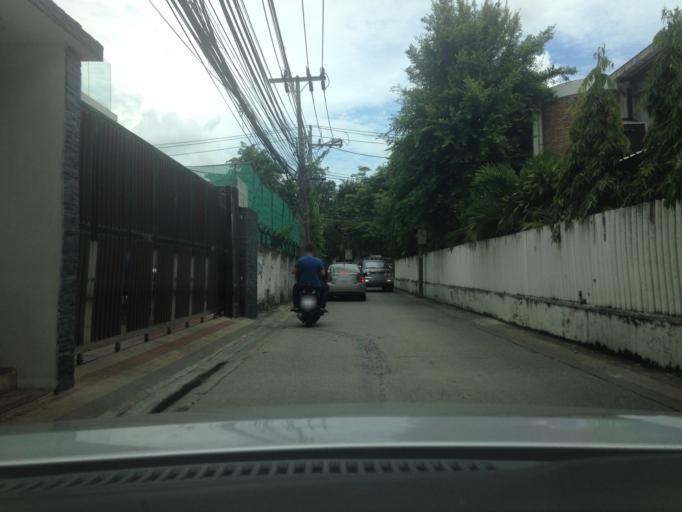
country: TH
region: Bangkok
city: Phaya Thai
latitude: 13.7870
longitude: 100.5443
